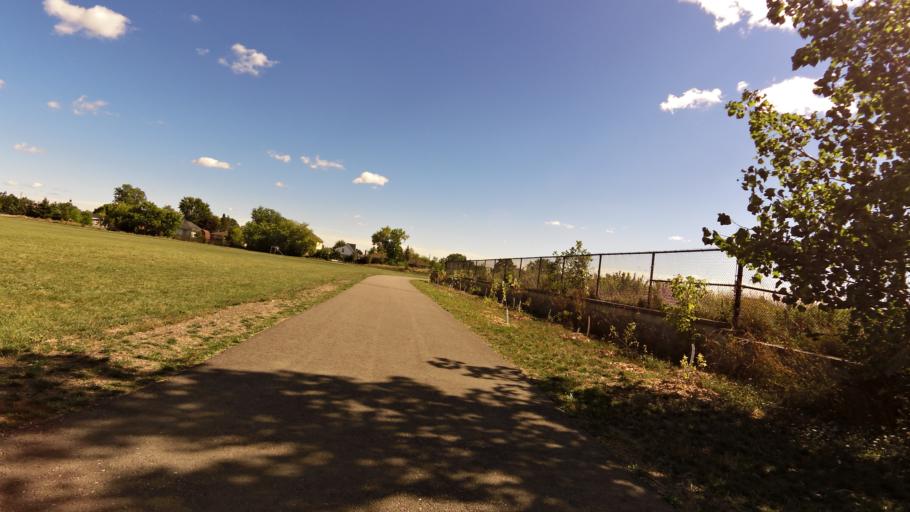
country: CA
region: Ontario
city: Etobicoke
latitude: 43.7073
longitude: -79.6510
